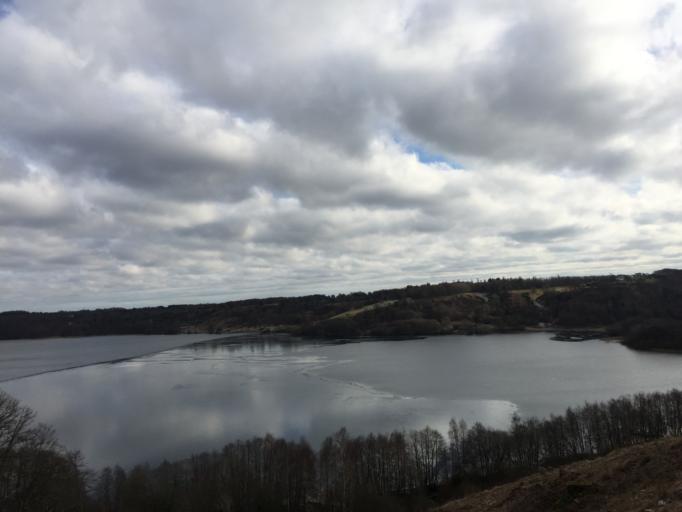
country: DK
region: Central Jutland
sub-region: Viborg Kommune
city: Viborg
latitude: 56.3719
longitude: 9.3242
